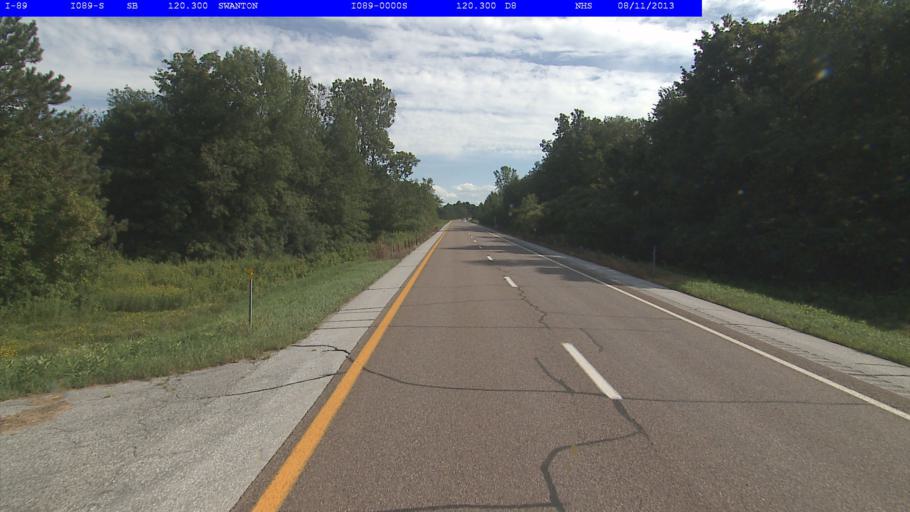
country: US
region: Vermont
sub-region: Franklin County
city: Swanton
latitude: 44.8811
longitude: -73.0848
